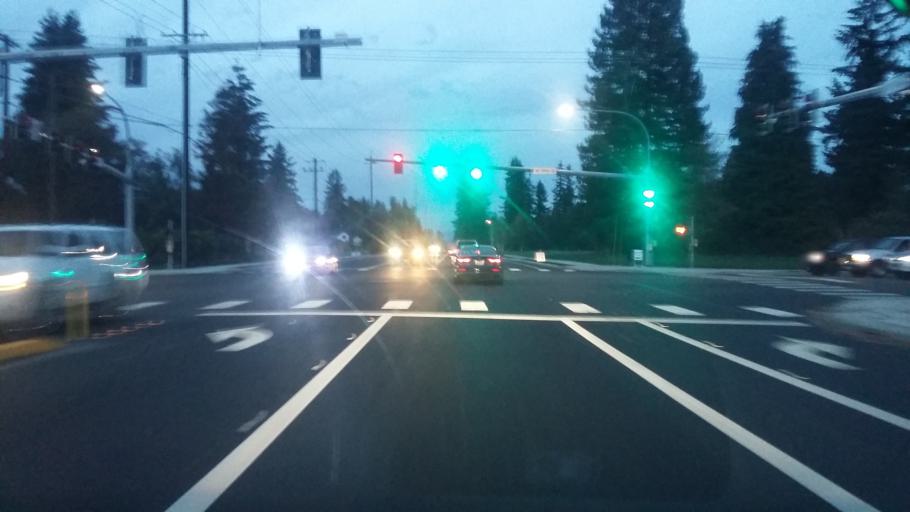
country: US
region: Washington
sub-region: Clark County
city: Barberton
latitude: 45.7074
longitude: -122.5994
